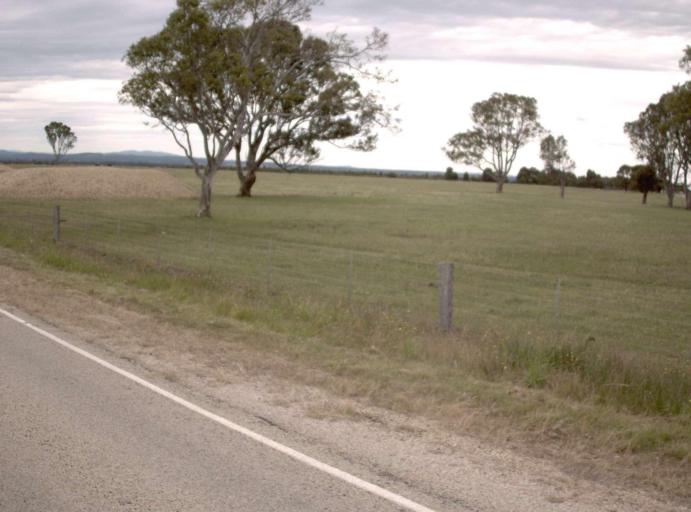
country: AU
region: Victoria
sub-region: East Gippsland
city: Bairnsdale
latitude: -37.8775
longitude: 147.5596
